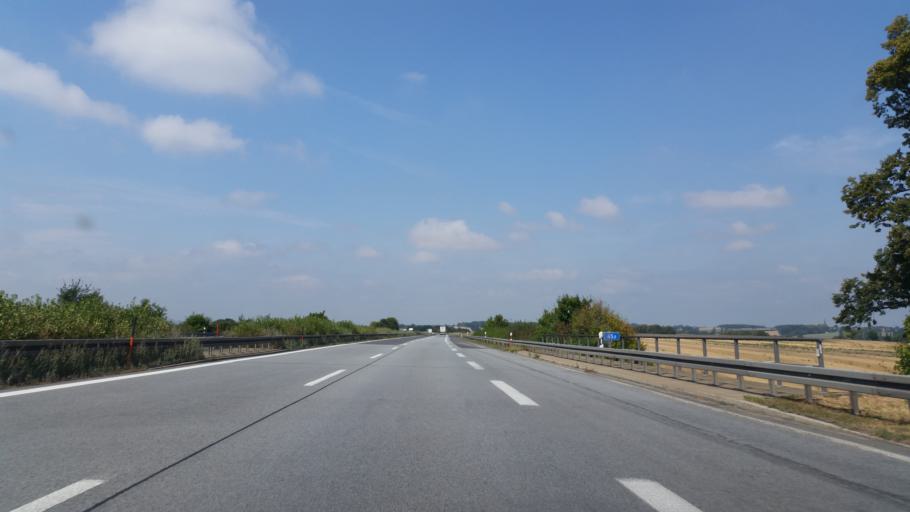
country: DE
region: Saxony
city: Goda
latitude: 51.2002
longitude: 14.3254
